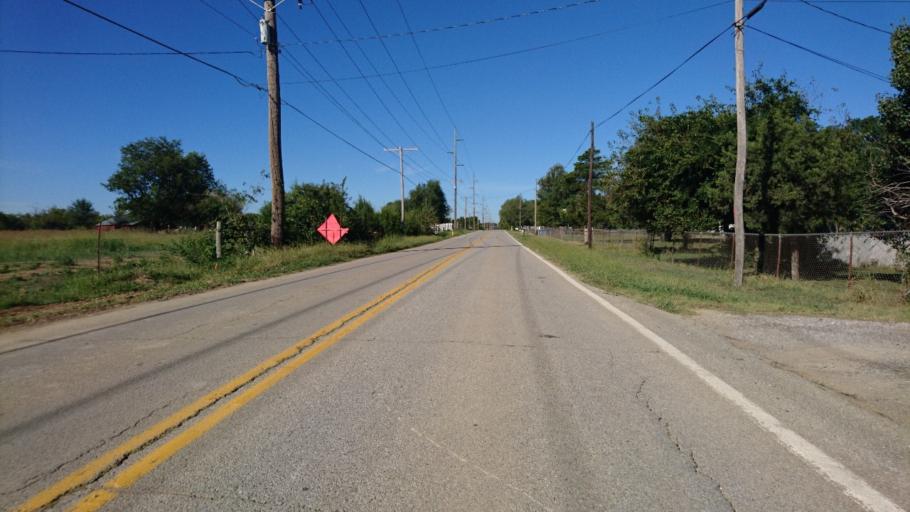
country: US
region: Oklahoma
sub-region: Rogers County
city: Catoosa
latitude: 36.1480
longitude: -95.7713
